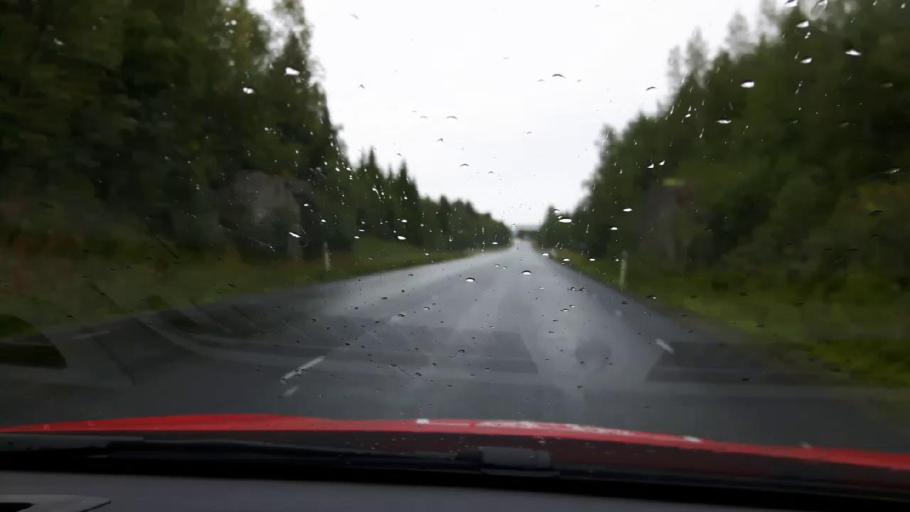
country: SE
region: Jaemtland
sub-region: Are Kommun
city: Are
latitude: 63.3968
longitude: 12.8548
